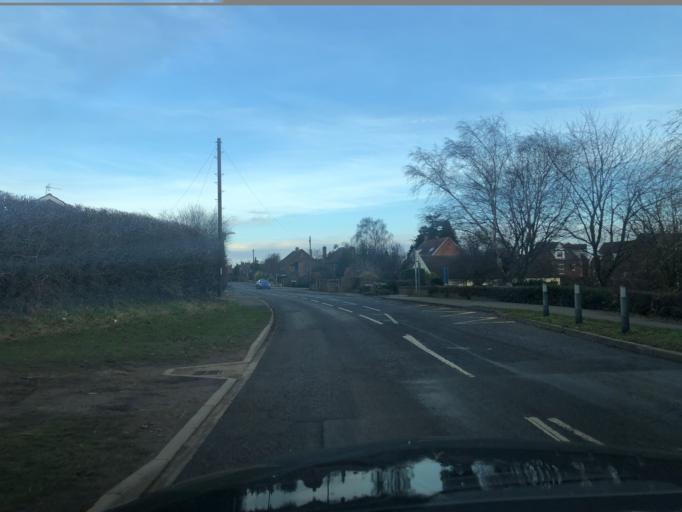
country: GB
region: England
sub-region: North Yorkshire
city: Bedale
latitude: 54.2834
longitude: -1.5995
